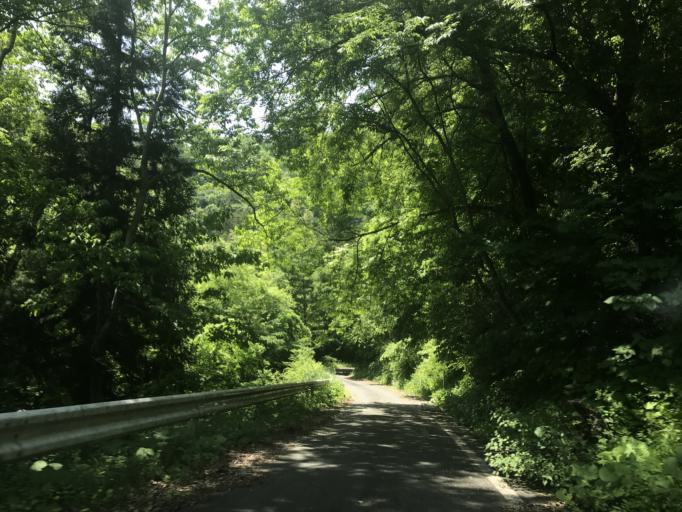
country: JP
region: Iwate
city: Ichinoseki
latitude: 38.9532
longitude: 141.2434
